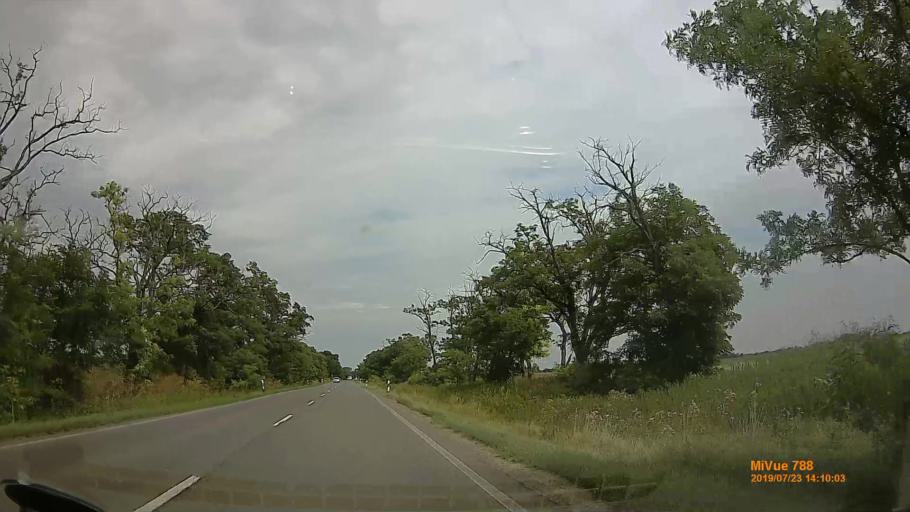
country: HU
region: Szabolcs-Szatmar-Bereg
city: Tiszavasvari
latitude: 47.9584
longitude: 21.4087
